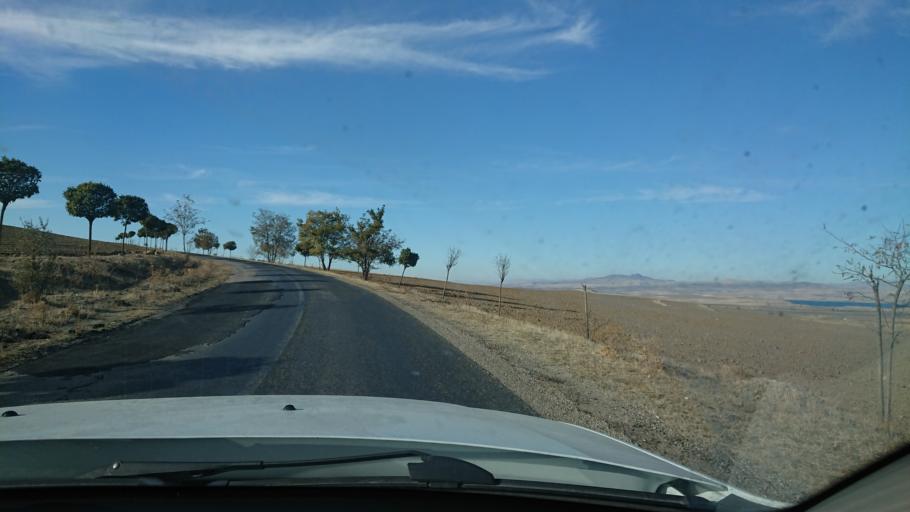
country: TR
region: Aksaray
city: Sariyahsi
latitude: 38.9710
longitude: 33.8661
